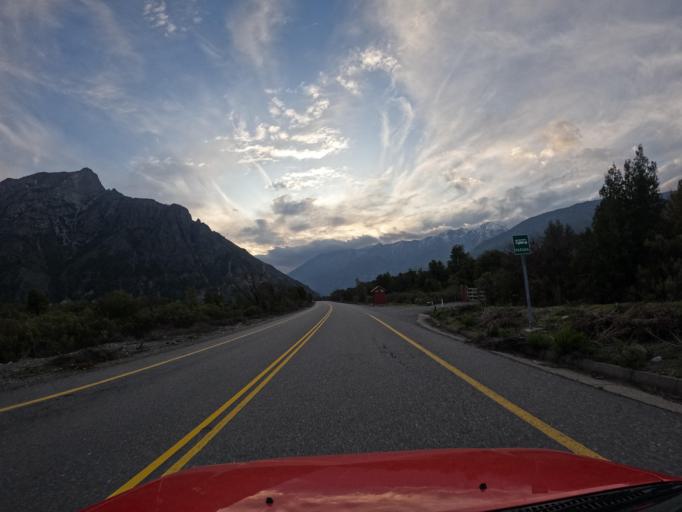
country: CL
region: Maule
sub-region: Provincia de Linares
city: Colbun
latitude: -35.7100
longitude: -71.0648
